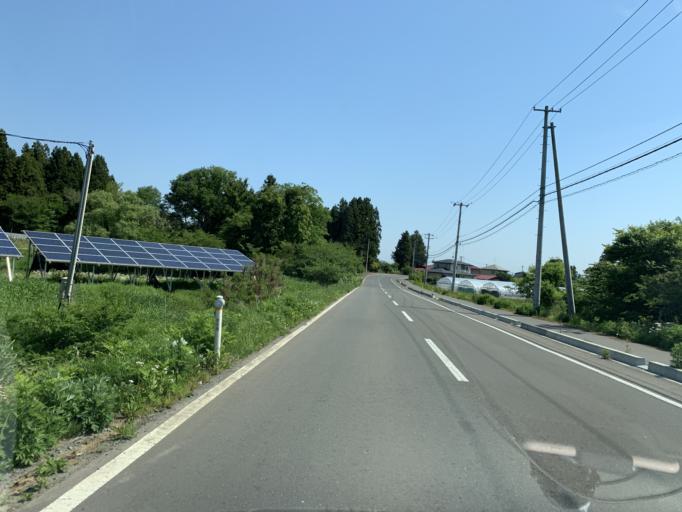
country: JP
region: Iwate
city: Mizusawa
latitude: 39.0901
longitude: 141.0701
